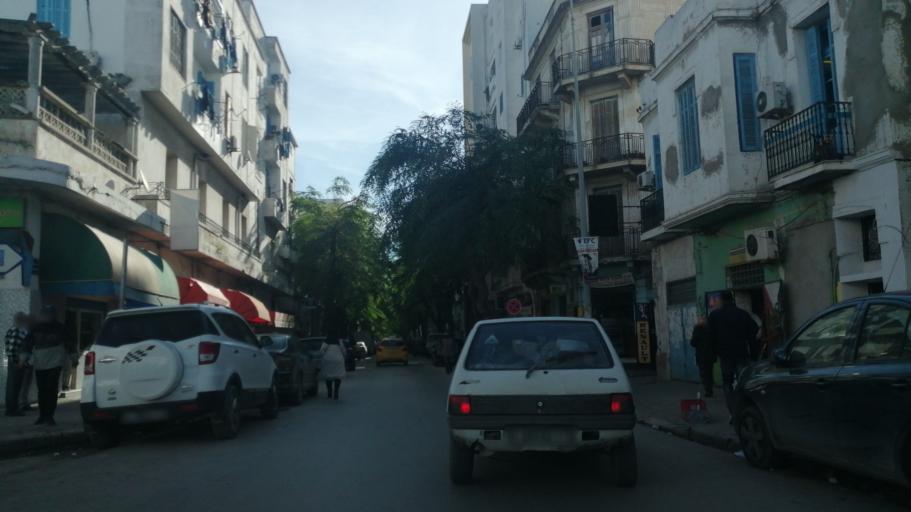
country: TN
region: Tunis
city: Tunis
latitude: 36.8093
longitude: 10.1747
